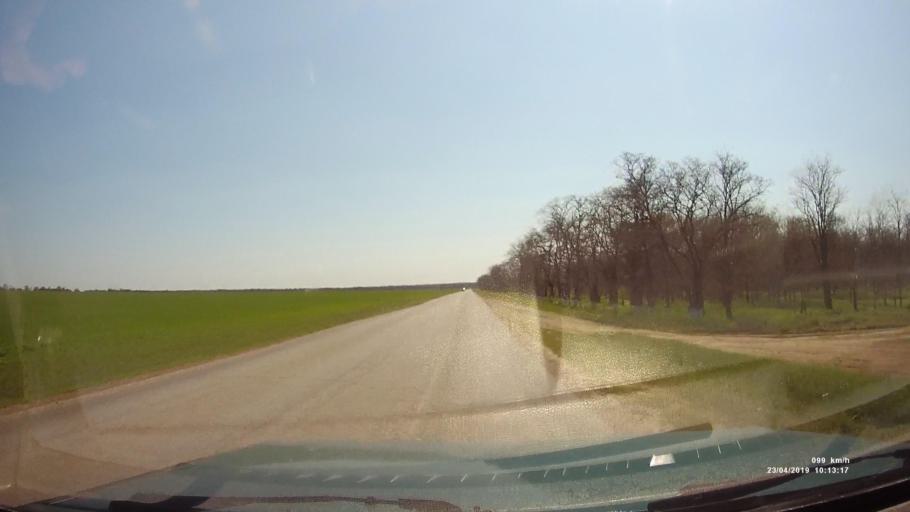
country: RU
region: Rostov
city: Sovetskoye
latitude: 46.6856
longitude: 42.3523
